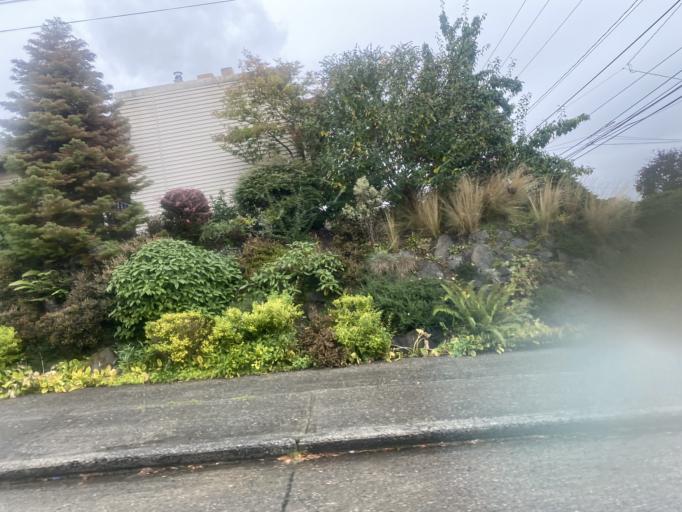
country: US
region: Washington
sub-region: King County
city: Seattle
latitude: 47.6423
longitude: -122.3926
